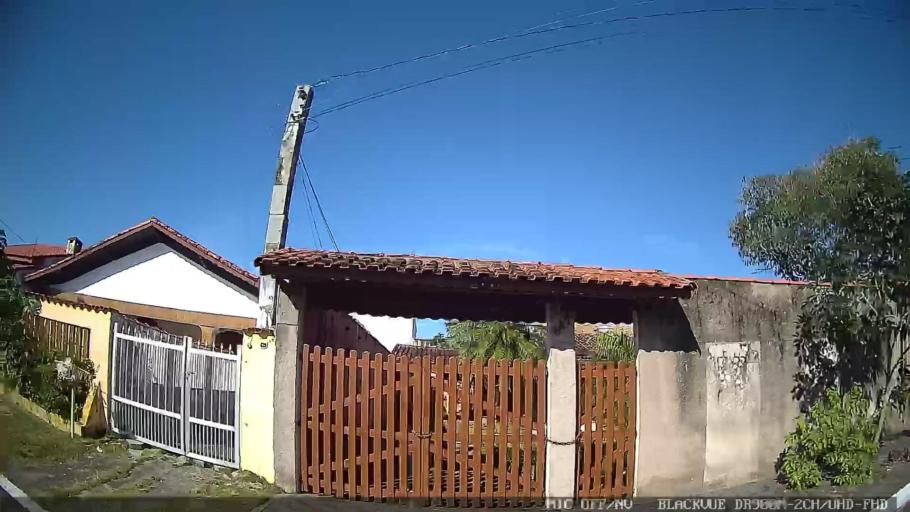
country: BR
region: Sao Paulo
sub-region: Peruibe
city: Peruibe
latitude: -24.2792
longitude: -46.9503
